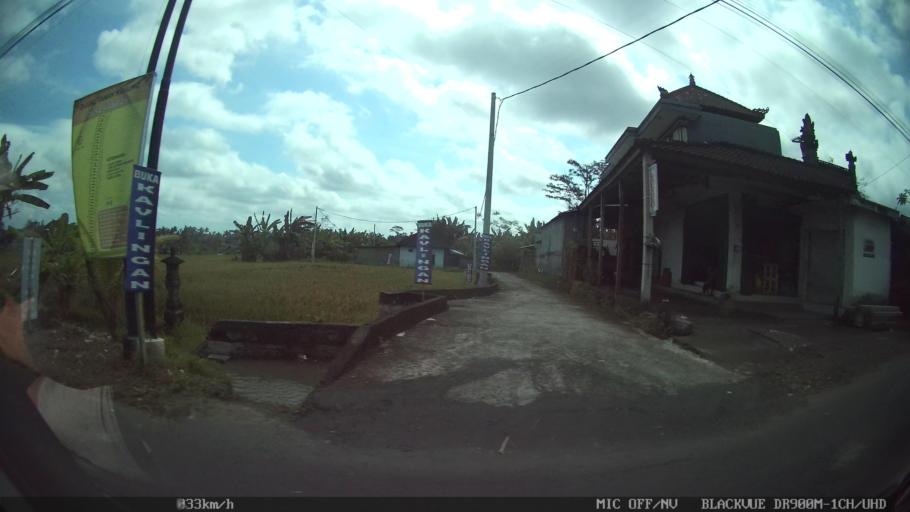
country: ID
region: Bali
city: Banjar Pesalakan
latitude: -8.5127
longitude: 115.3125
